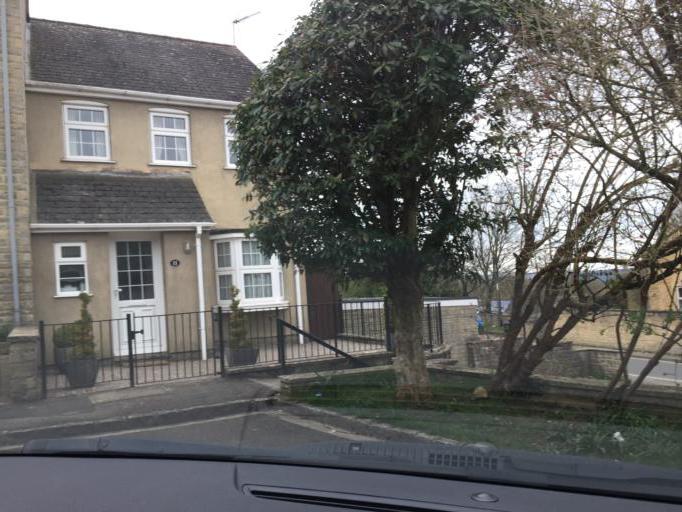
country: GB
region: England
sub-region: Oxfordshire
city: Chipping Norton
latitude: 51.9407
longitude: -1.5471
